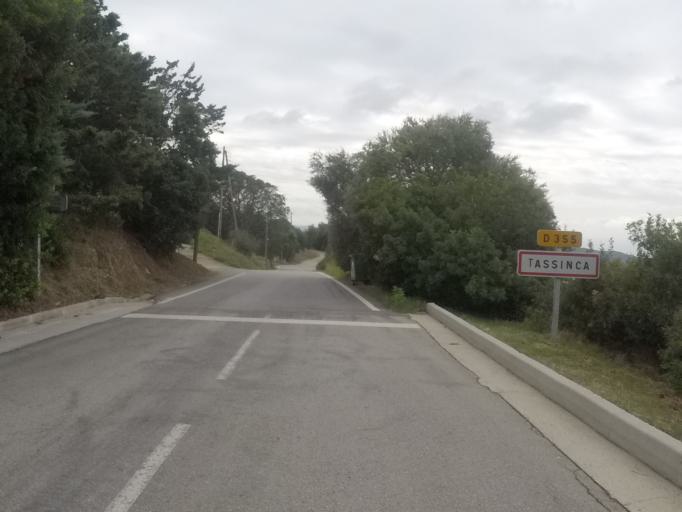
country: FR
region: Corsica
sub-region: Departement de la Corse-du-Sud
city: Pietrosella
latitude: 41.7616
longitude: 8.8132
